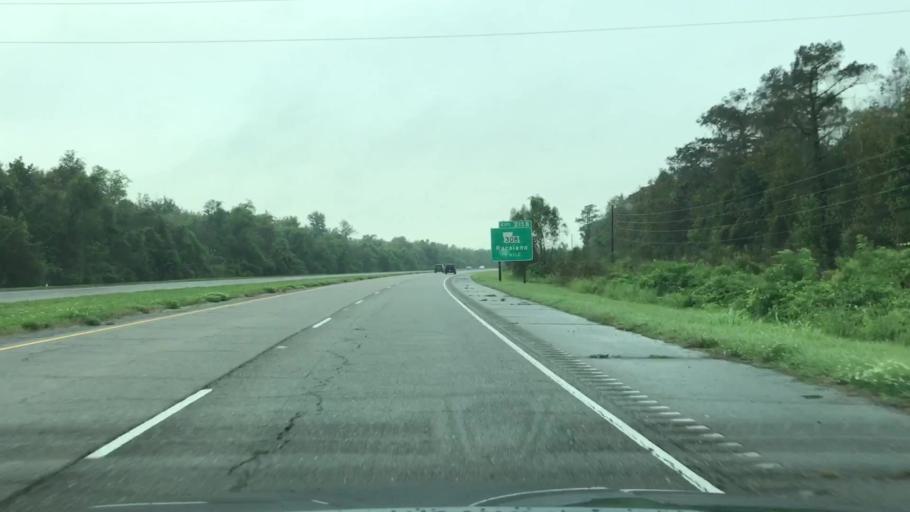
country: US
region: Louisiana
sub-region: Lafourche Parish
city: Raceland
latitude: 29.7244
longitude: -90.5596
